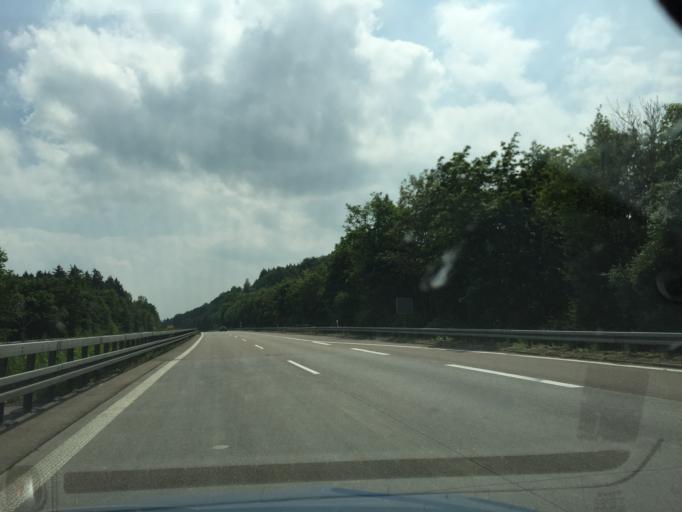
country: DE
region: Baden-Wuerttemberg
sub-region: Tuebingen Region
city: Nerenstetten
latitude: 48.5195
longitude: 10.0818
